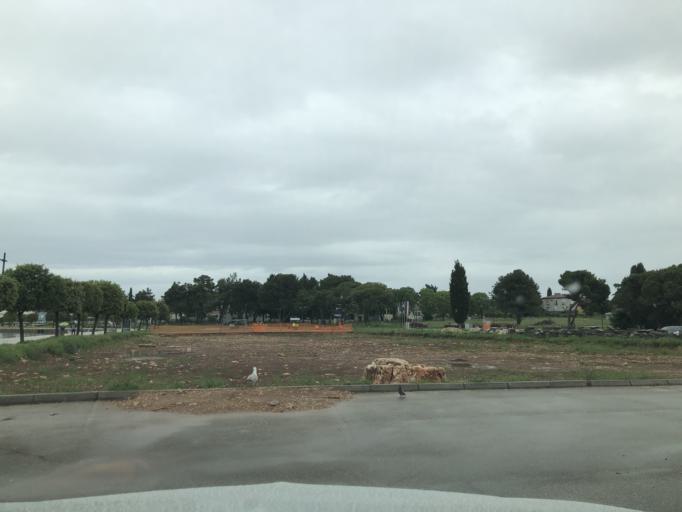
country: HR
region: Istarska
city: Umag
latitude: 45.4357
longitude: 13.5234
